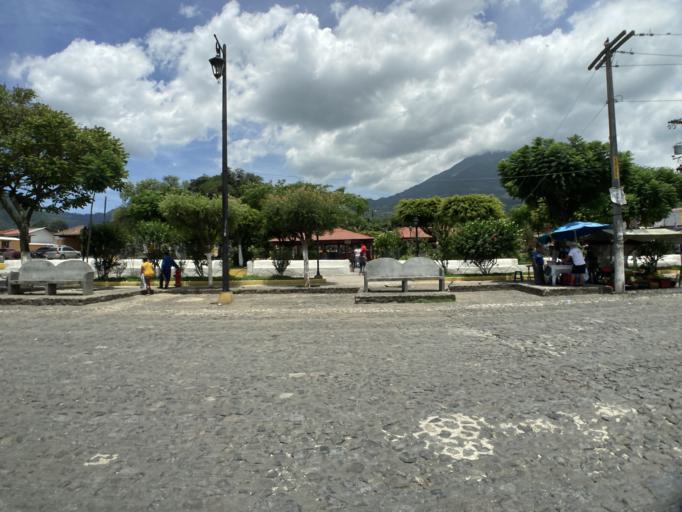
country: GT
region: Sacatepequez
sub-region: Municipio de Santa Maria de Jesus
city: Santa Maria de Jesus
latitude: 14.5306
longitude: -90.7402
